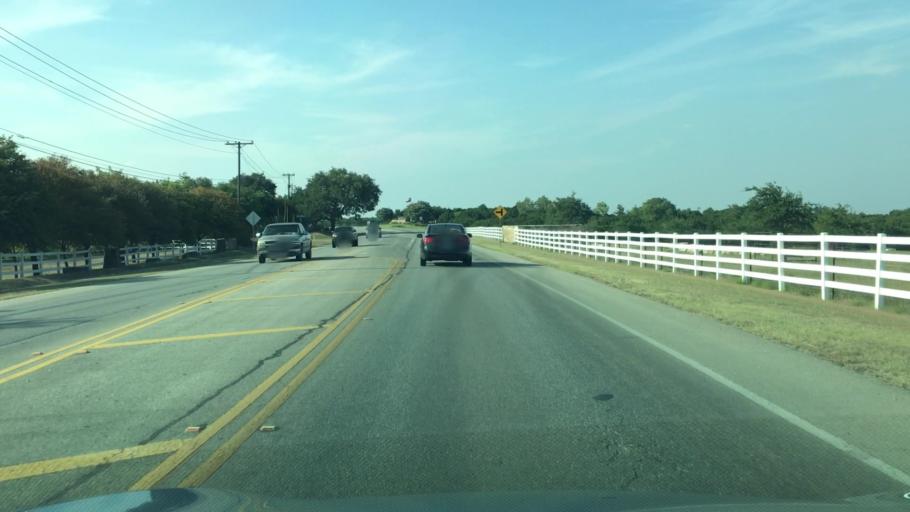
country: US
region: Texas
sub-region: Hays County
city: Dripping Springs
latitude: 30.1849
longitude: -98.0009
